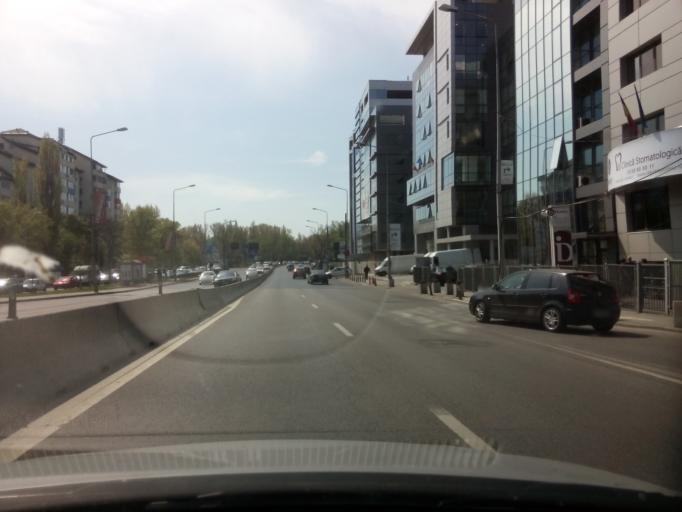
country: RO
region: Ilfov
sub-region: Comuna Otopeni
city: Otopeni
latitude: 44.4919
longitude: 26.0791
